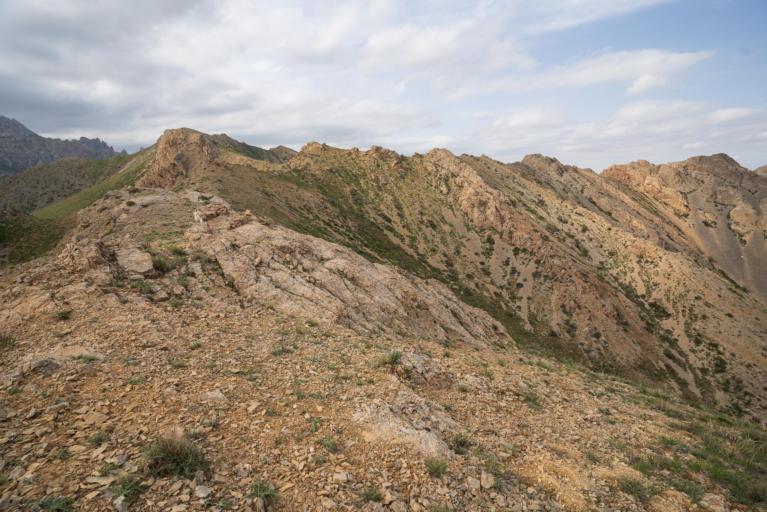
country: KZ
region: Ongtustik Qazaqstan
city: Ashchysay
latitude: 43.7500
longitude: 68.8242
